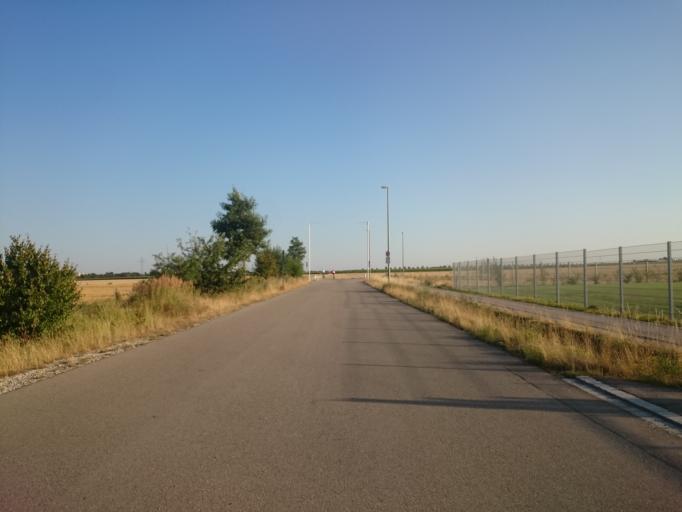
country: DE
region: Bavaria
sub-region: Swabia
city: Konigsbrunn
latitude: 48.3204
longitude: 10.8802
